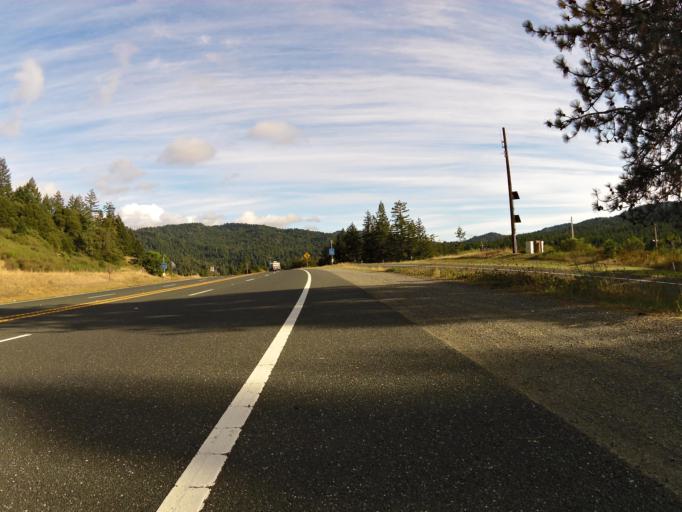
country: US
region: California
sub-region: Humboldt County
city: Redway
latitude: 39.9653
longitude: -123.7949
